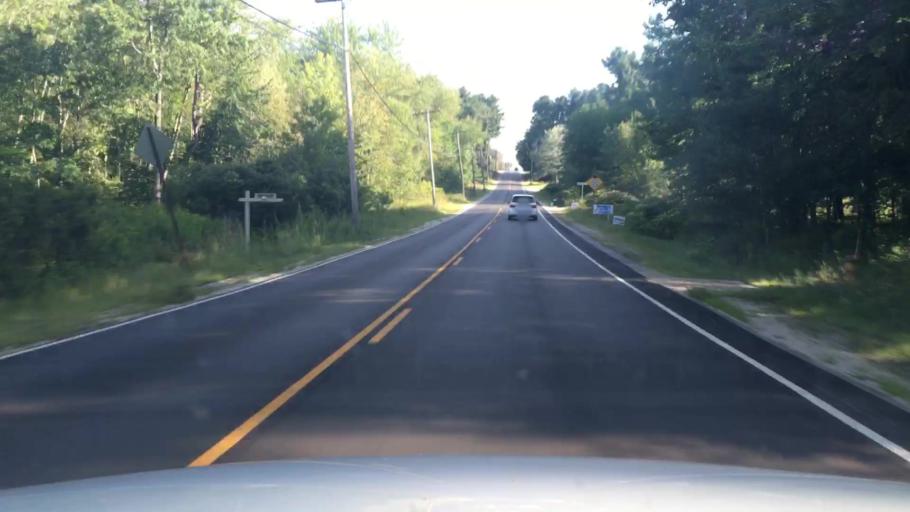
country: US
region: Maine
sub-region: Cumberland County
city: Cumberland Center
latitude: 43.8223
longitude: -70.3155
